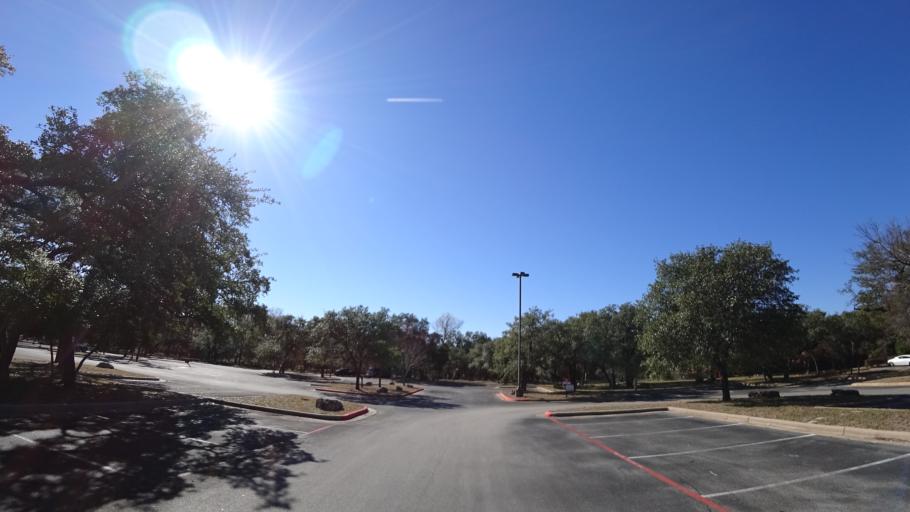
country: US
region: Texas
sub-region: Travis County
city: Wells Branch
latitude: 30.4244
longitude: -97.7163
